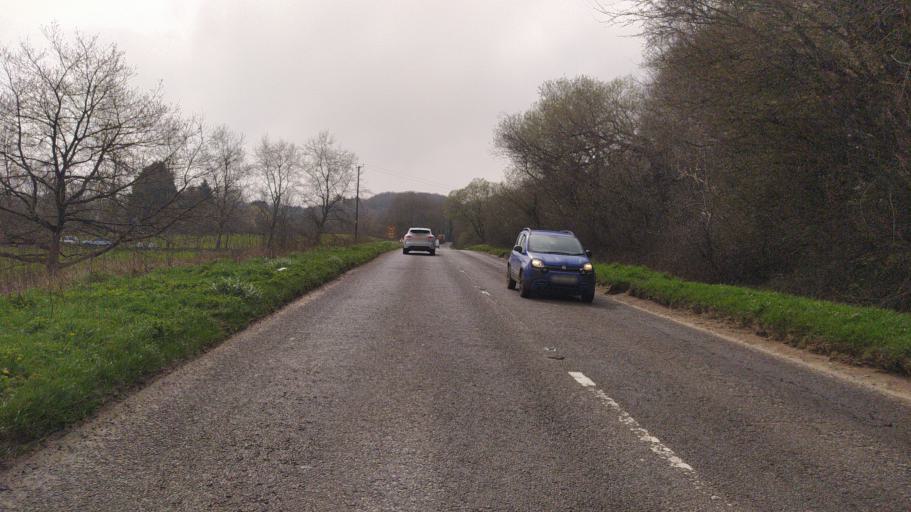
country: GB
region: England
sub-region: Dorset
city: Shaftesbury
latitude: 51.0363
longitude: -2.1850
